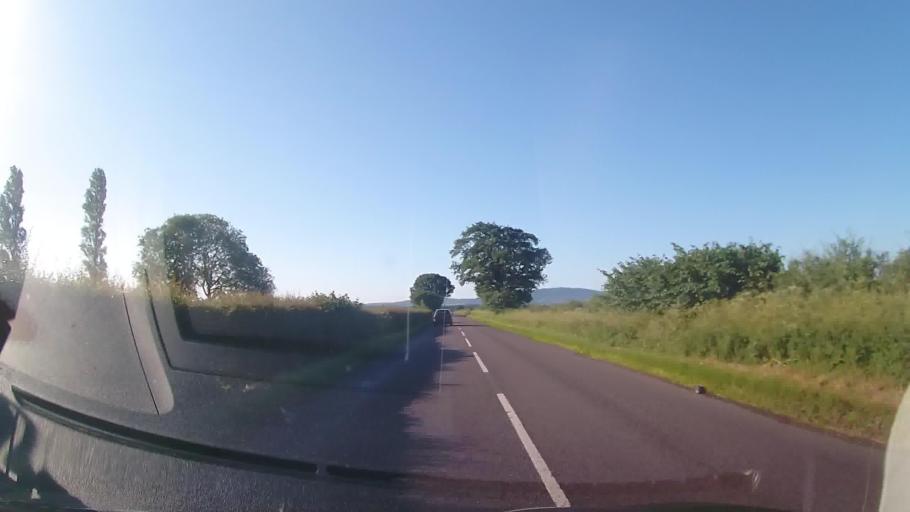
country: GB
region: England
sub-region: Shropshire
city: Withington
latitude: 52.7511
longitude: -2.5895
